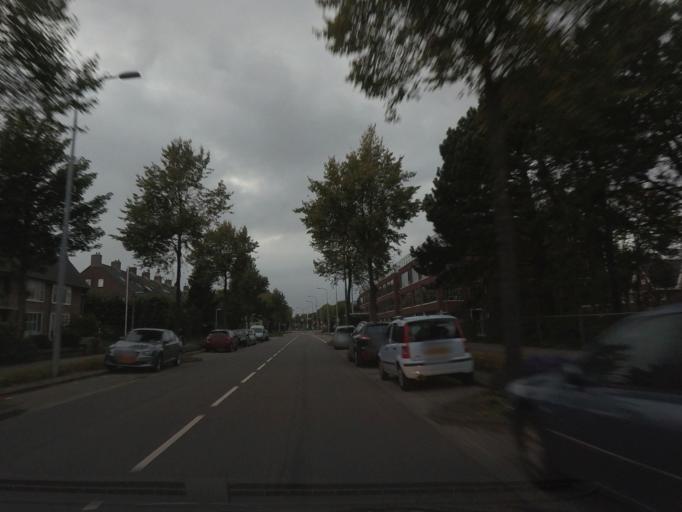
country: NL
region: North Holland
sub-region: Gemeente Alkmaar
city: Alkmaar
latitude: 52.6383
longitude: 4.7319
